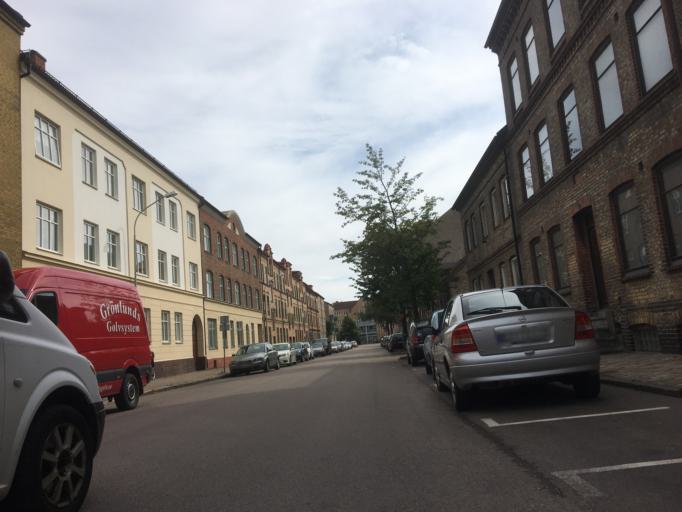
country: SE
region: Skane
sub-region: Landskrona
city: Landskrona
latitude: 55.8779
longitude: 12.8305
